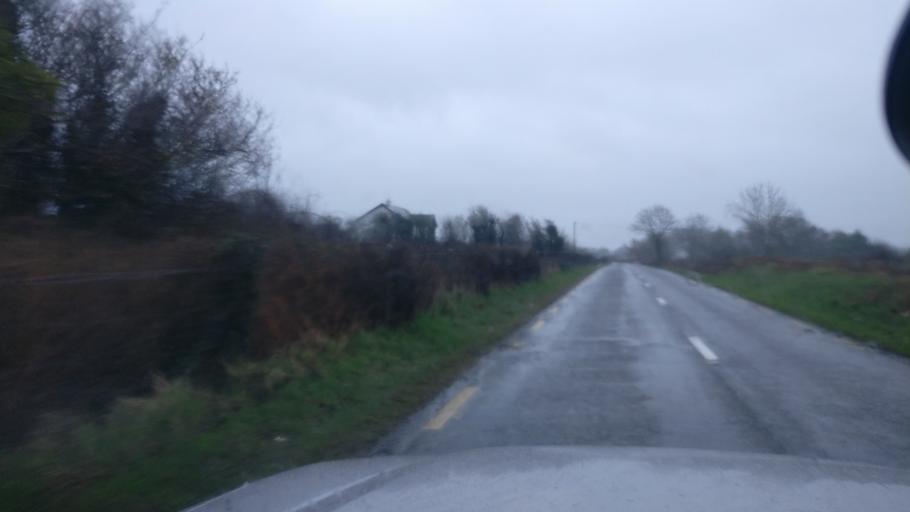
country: IE
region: Connaught
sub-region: County Galway
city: Ballinasloe
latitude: 53.2741
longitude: -8.2050
